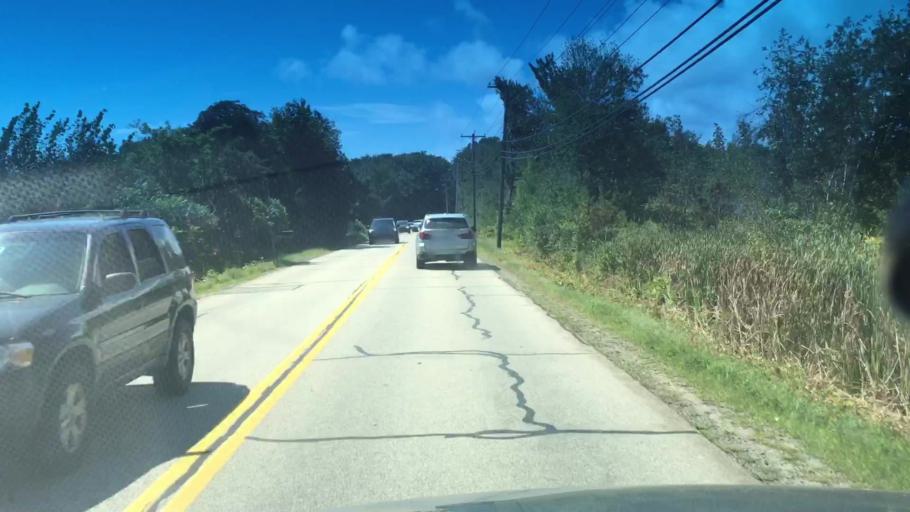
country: US
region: Maine
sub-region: York County
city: York Beach
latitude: 43.1607
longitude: -70.6288
